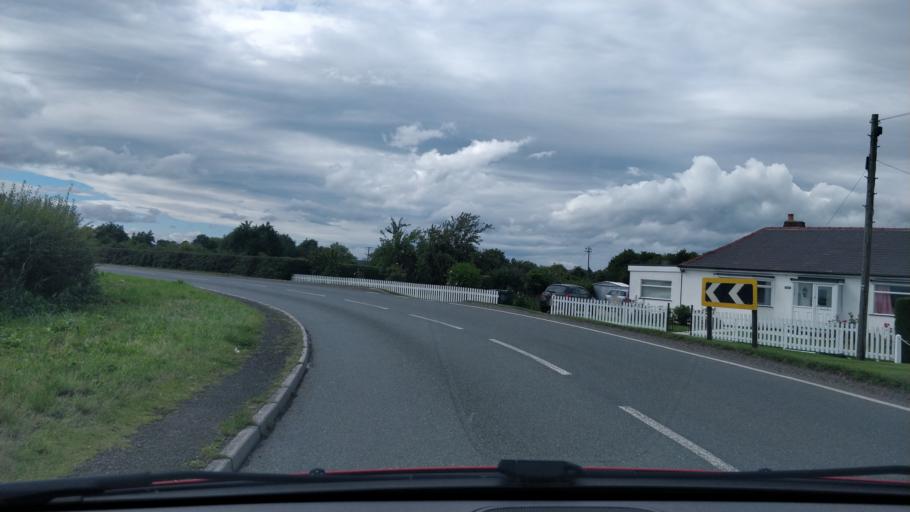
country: GB
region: England
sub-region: Cheshire West and Chester
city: Eccleston
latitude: 53.1550
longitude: -2.9187
